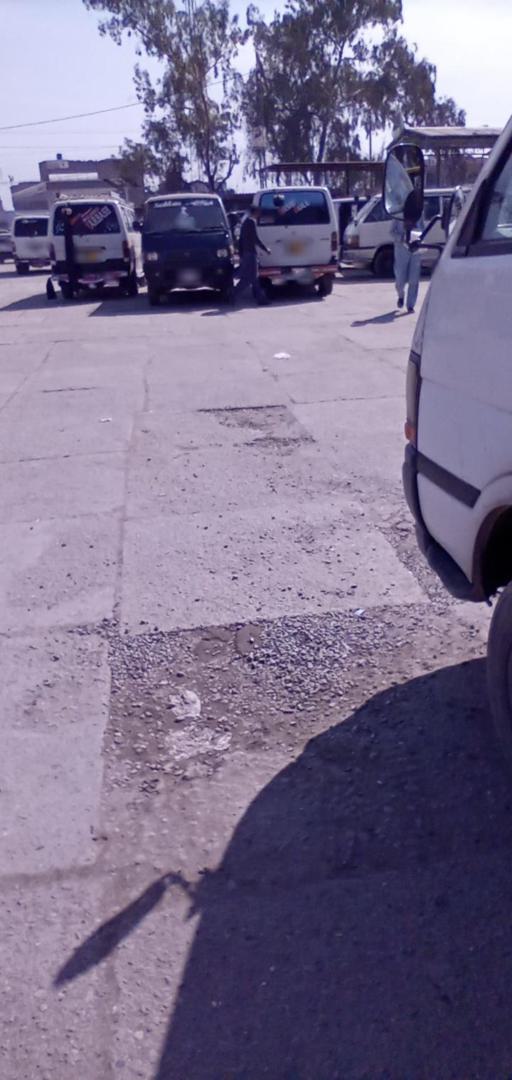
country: PK
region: Khyber Pakhtunkhwa
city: Peshawar
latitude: 33.9694
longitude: 71.5615
